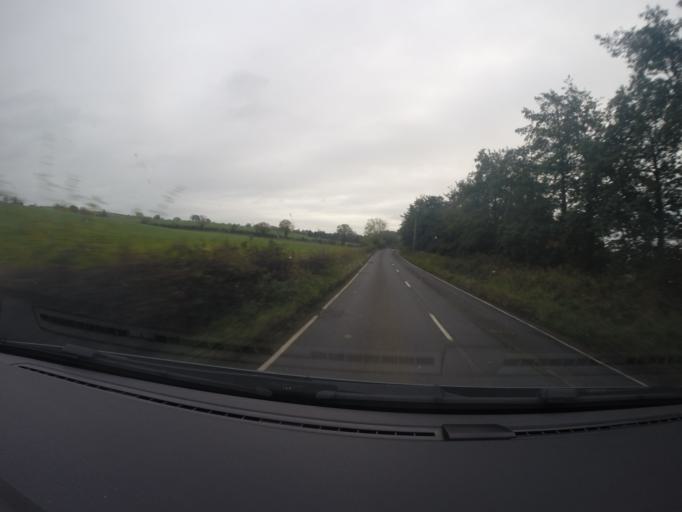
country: GB
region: Northern Ireland
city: Annahilt
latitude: 54.4881
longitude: -5.9734
